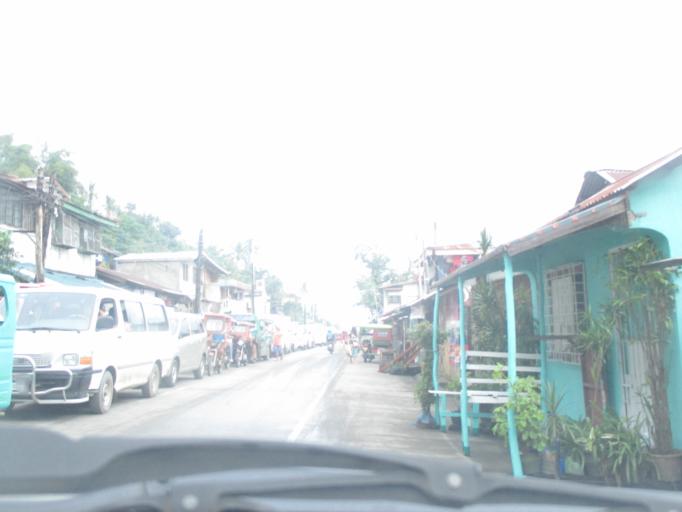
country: PH
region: Eastern Visayas
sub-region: Province of Leyte
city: Panalanoy
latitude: 11.2465
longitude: 124.9946
